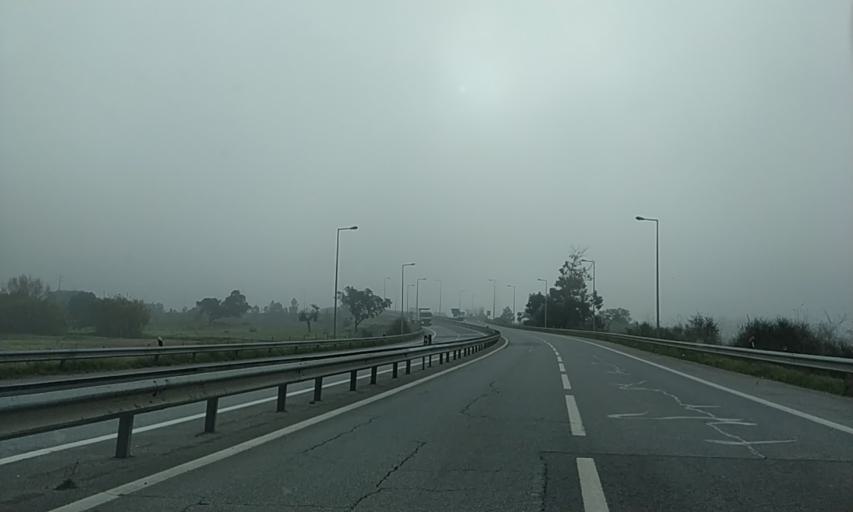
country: PT
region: Setubal
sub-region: Montijo
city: Montijo
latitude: 38.6813
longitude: -8.9479
